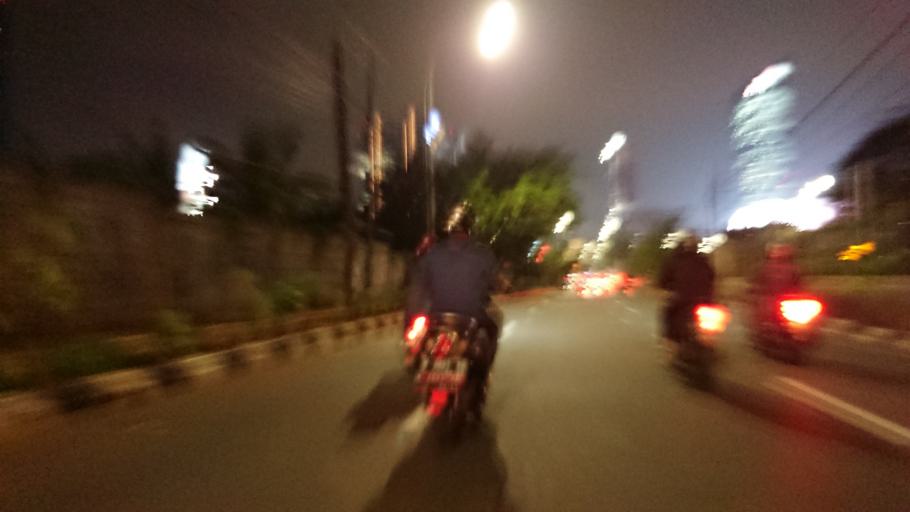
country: ID
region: Jakarta Raya
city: Jakarta
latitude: -6.2047
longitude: 106.7991
